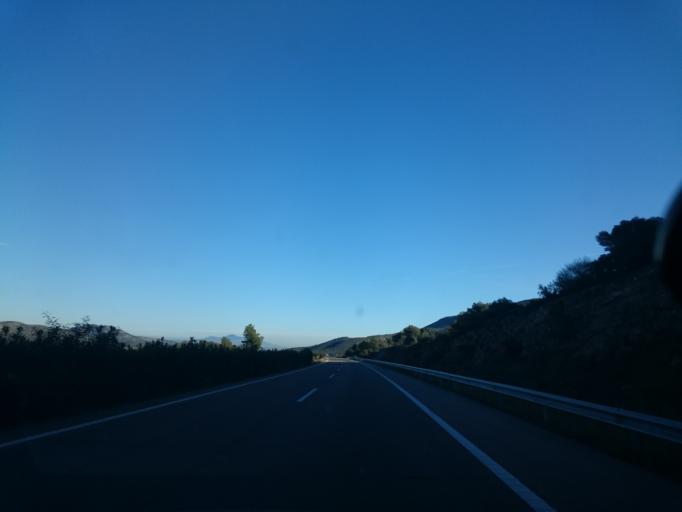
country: ES
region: Valencia
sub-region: Provincia de Castello
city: Santa Magdalena de Pulpis
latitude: 40.3569
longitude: 0.3161
